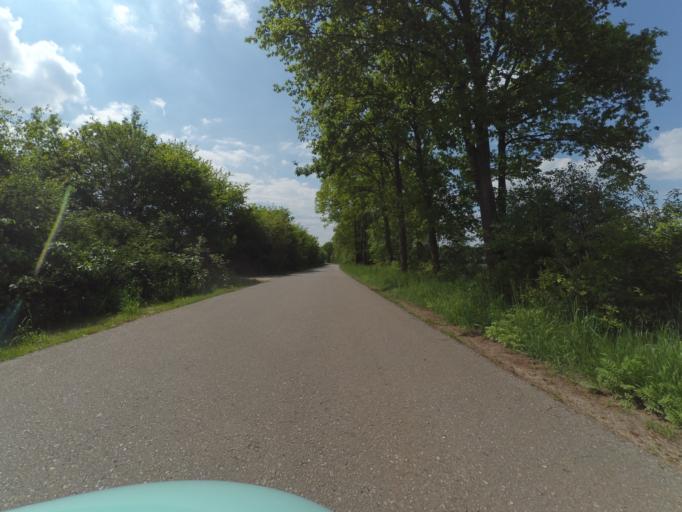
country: DE
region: Lower Saxony
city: Meinersen
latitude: 52.4533
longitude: 10.2942
